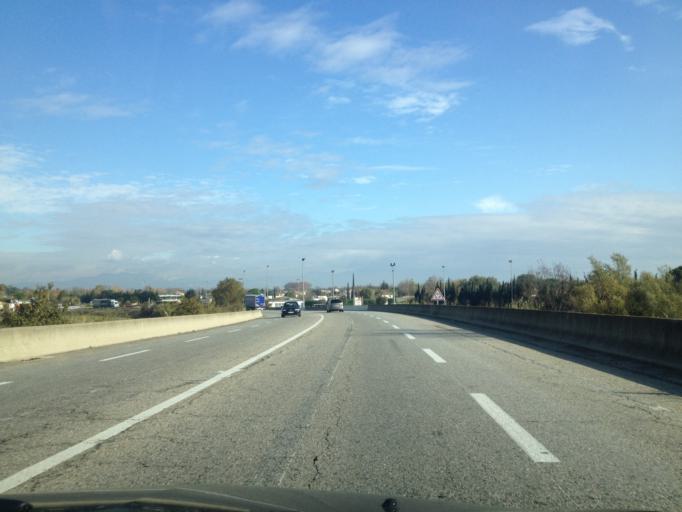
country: FR
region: Provence-Alpes-Cote d'Azur
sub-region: Departement du Vaucluse
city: Bedarrides
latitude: 44.0382
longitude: 4.8847
